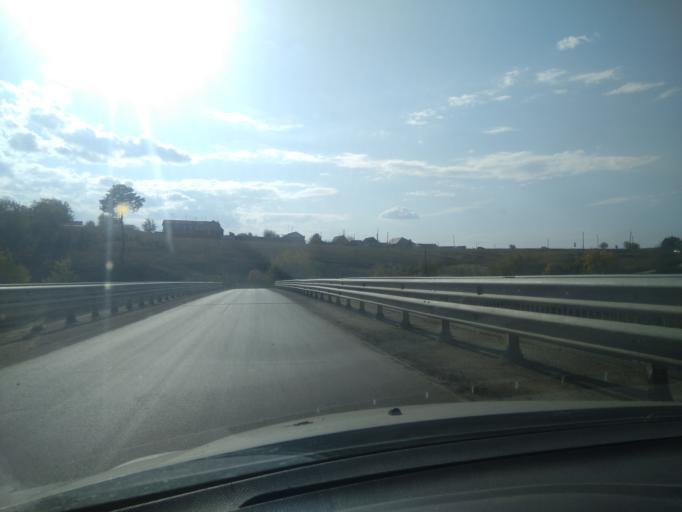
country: RU
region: Sverdlovsk
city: Pokrovskoye
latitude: 56.4365
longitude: 61.5927
